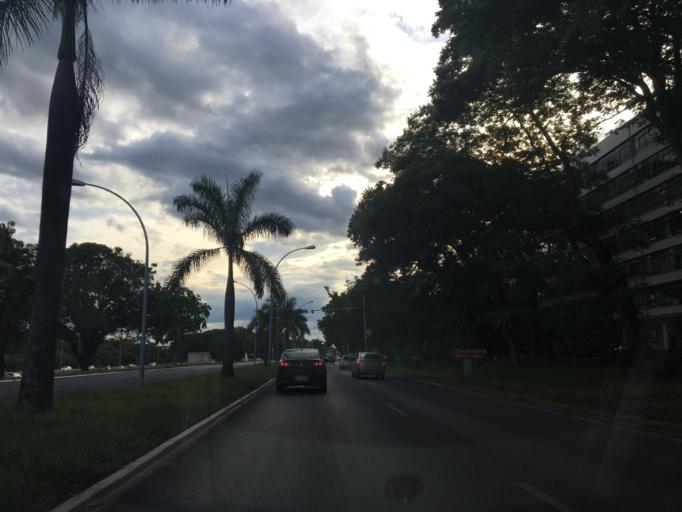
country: BR
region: Federal District
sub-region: Brasilia
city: Brasilia
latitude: -15.8136
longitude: -47.8976
